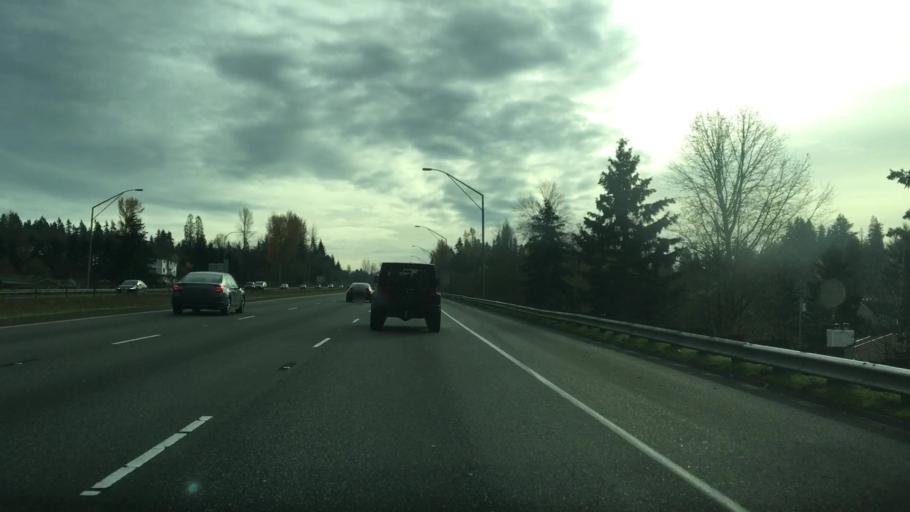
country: US
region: Washington
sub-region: Pierce County
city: Puyallup
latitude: 47.1729
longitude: -122.2971
